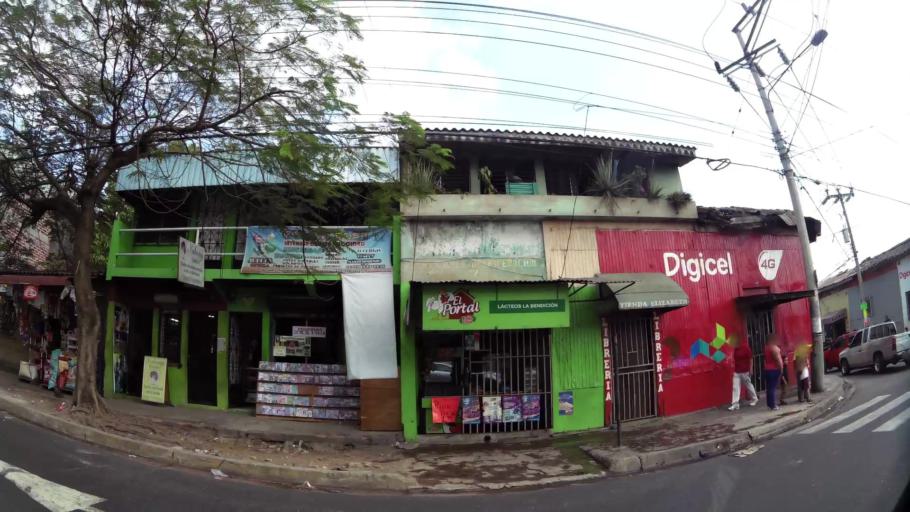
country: SV
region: San Salvador
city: Delgado
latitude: 13.7169
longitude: -89.1700
